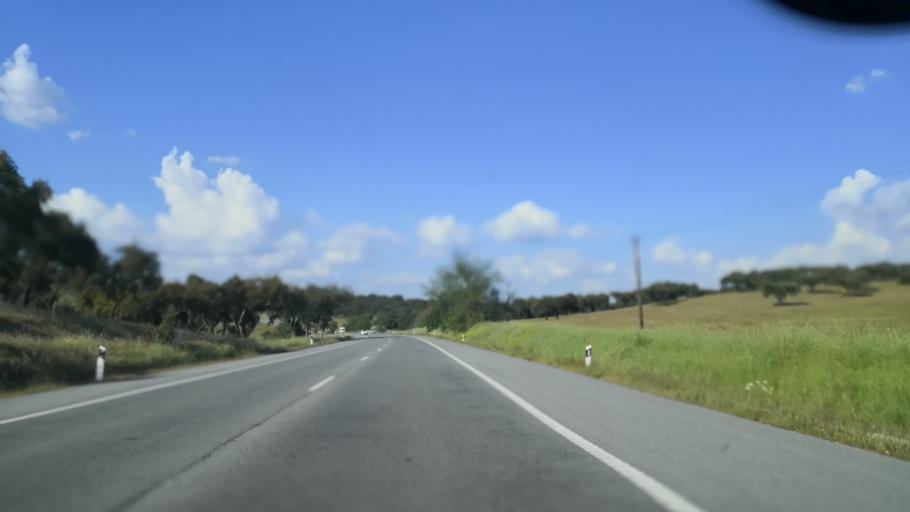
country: PT
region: Portalegre
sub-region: Fronteira
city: Fronteira
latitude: 39.0274
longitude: -7.4570
